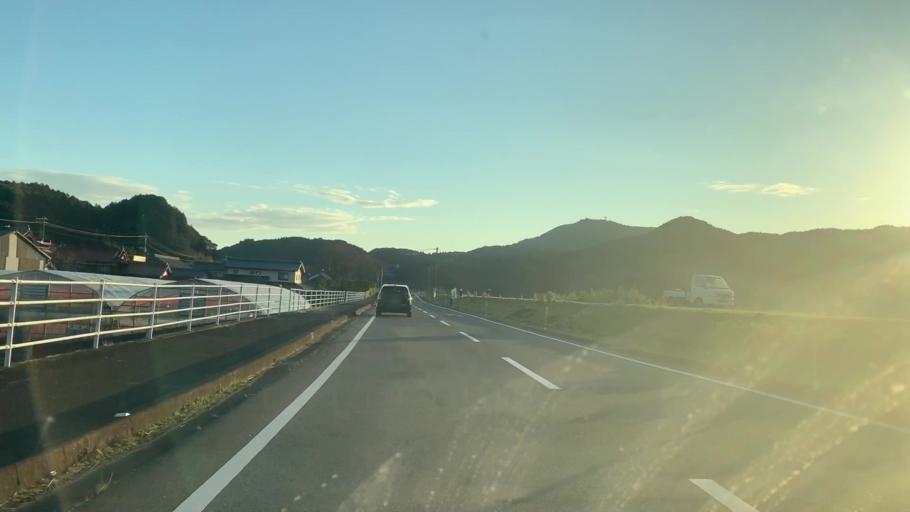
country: JP
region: Saga Prefecture
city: Imaricho-ko
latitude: 33.3069
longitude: 129.9690
